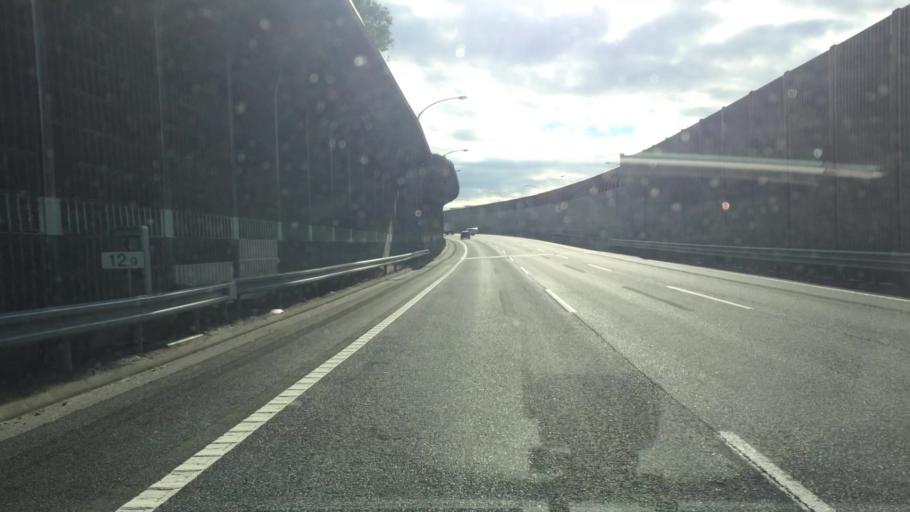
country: JP
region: Chiba
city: Chiba
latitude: 35.6443
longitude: 140.0691
